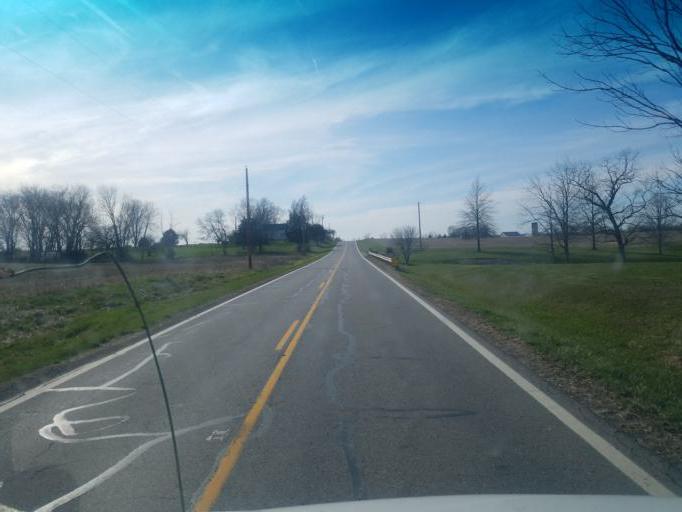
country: US
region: Ohio
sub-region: Champaign County
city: North Lewisburg
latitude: 40.3424
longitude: -83.4924
